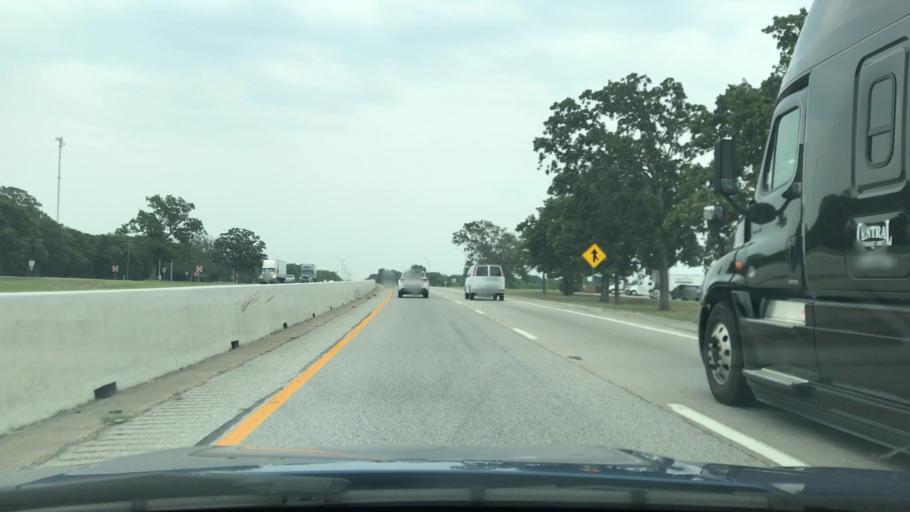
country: US
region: Texas
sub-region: Van Zandt County
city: Van
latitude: 32.5143
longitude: -95.6861
